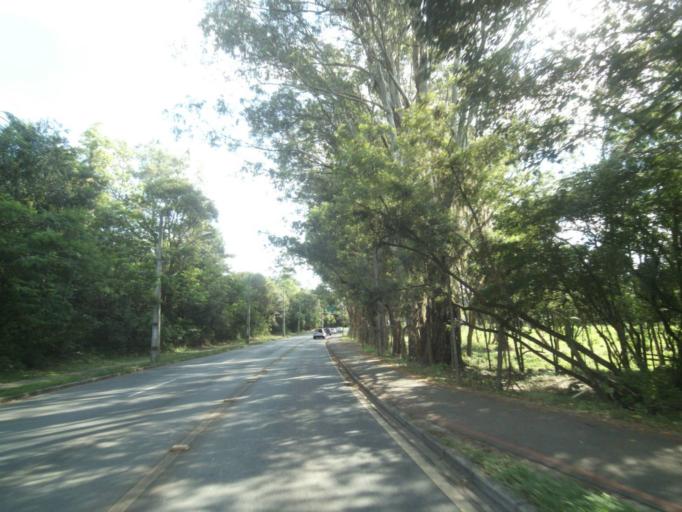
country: BR
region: Parana
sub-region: Curitiba
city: Curitiba
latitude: -25.3862
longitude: -49.3000
